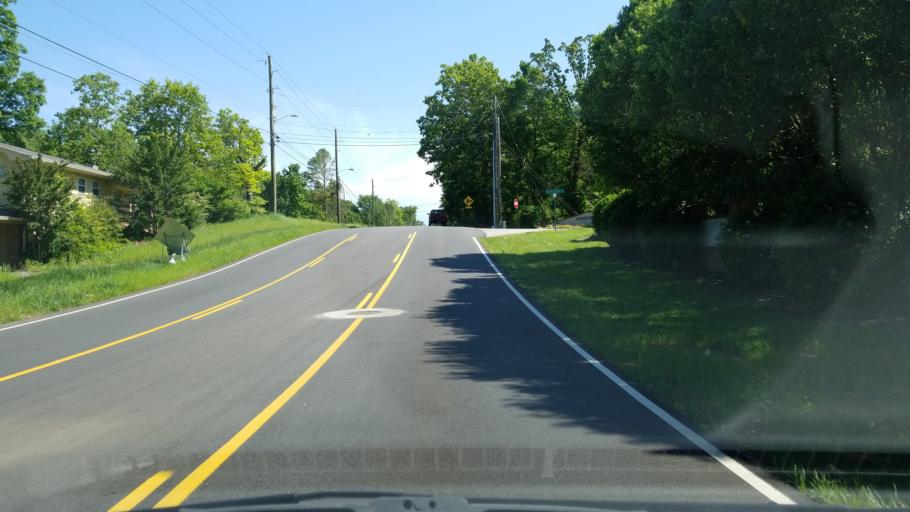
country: US
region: Tennessee
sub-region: Hamilton County
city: East Brainerd
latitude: 35.0440
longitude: -85.1480
